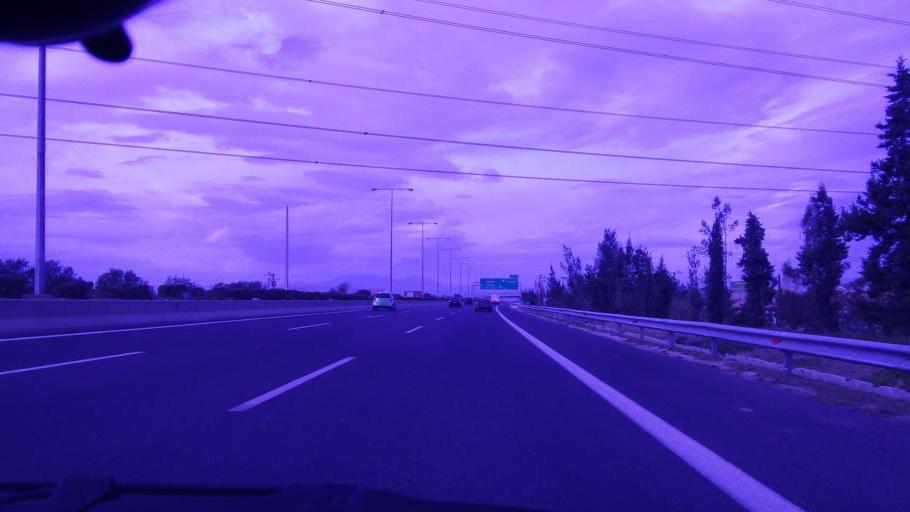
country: GR
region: Attica
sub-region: Nomarchia Dytikis Attikis
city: Fyli
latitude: 38.0875
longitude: 23.6338
